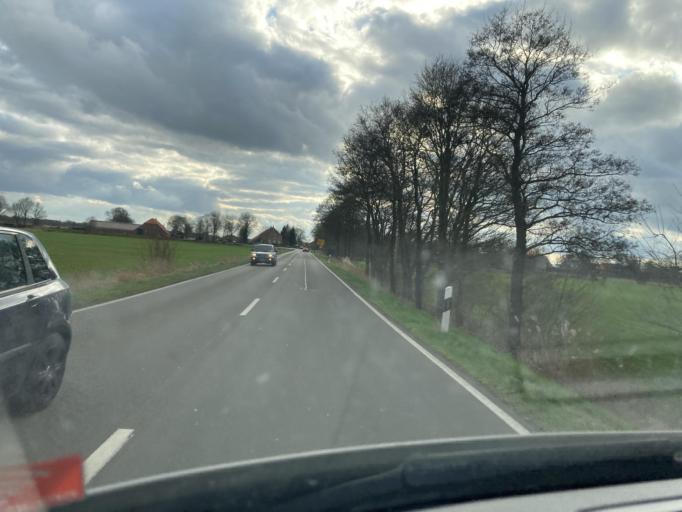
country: DE
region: Lower Saxony
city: Filsum
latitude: 53.1894
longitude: 7.6182
